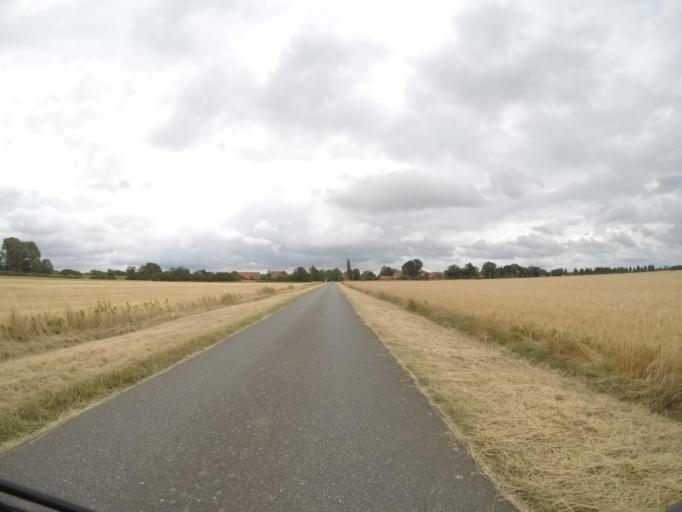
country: DE
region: Lower Saxony
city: Damnatz
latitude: 53.1680
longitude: 11.1225
